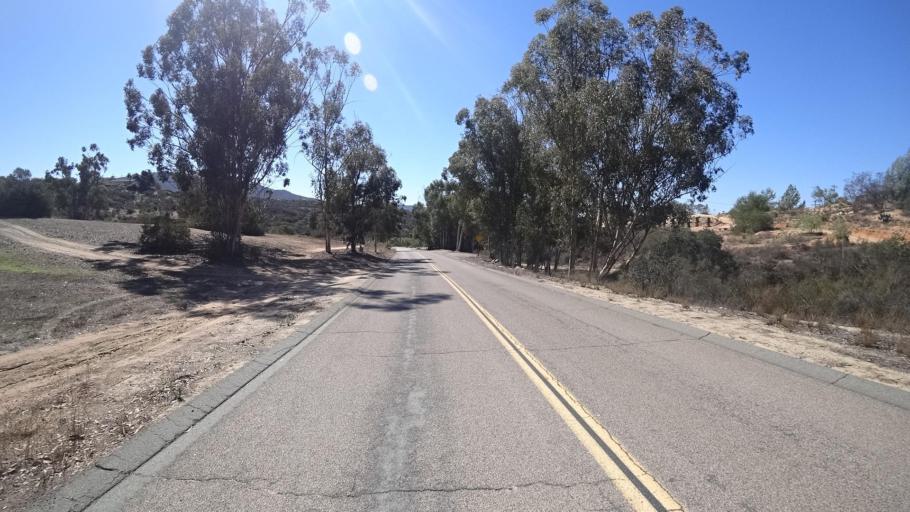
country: US
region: California
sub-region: San Diego County
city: Harbison Canyon
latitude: 32.7894
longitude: -116.8070
